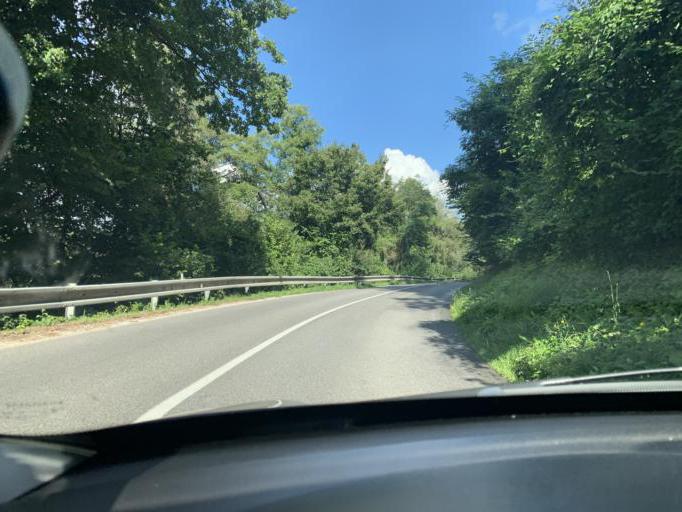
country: SK
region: Trenciansky
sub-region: Okres Nove Mesto nad Vahom
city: Nove Mesto nad Vahom
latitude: 48.8125
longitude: 17.9252
